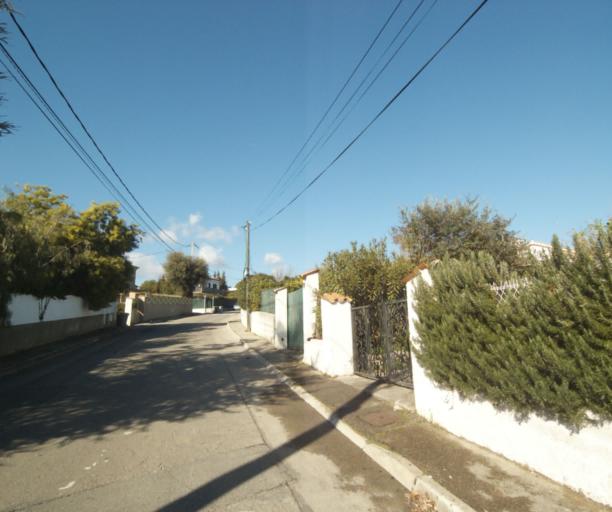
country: FR
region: Provence-Alpes-Cote d'Azur
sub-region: Departement des Alpes-Maritimes
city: Biot
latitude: 43.6180
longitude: 7.1220
